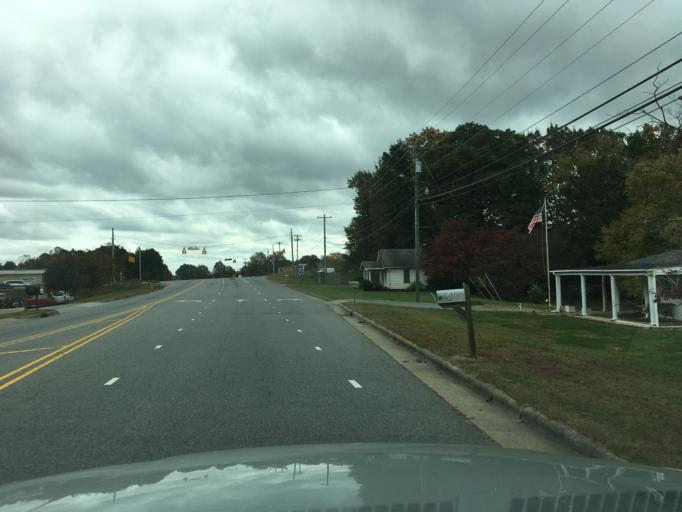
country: US
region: North Carolina
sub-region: Catawba County
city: Saint Stephens
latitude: 35.7234
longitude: -81.2949
